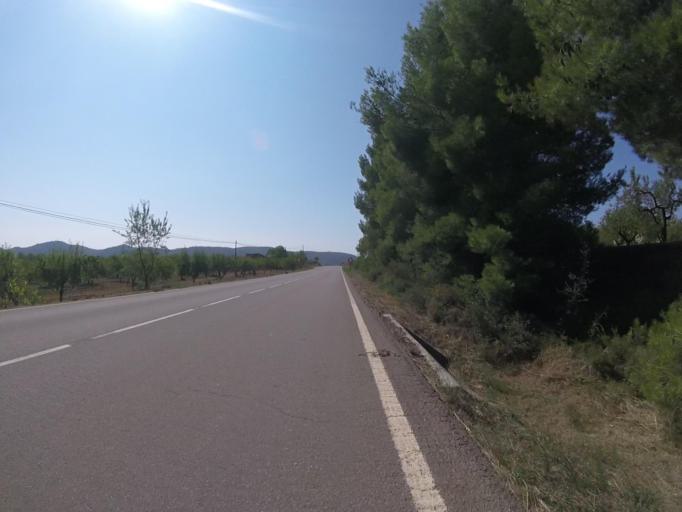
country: ES
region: Valencia
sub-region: Provincia de Castello
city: Adzaneta
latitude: 40.2317
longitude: -0.1768
